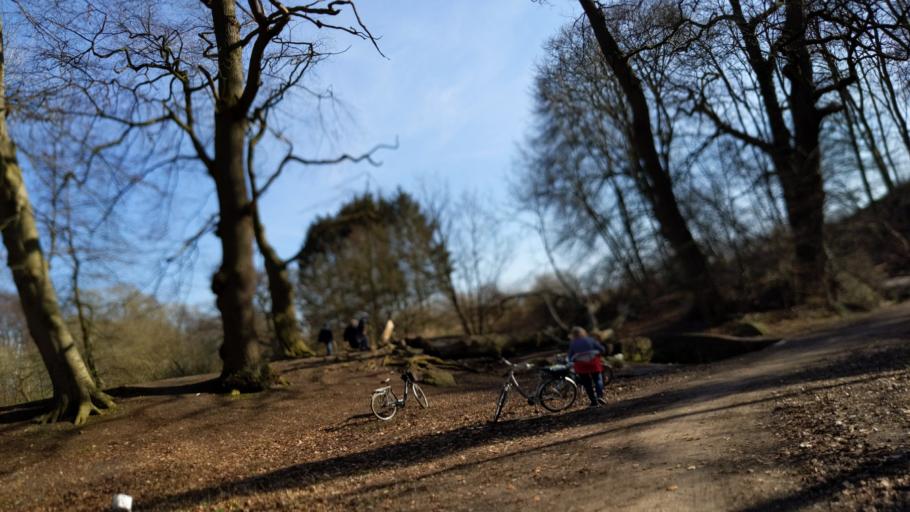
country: DE
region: Schleswig-Holstein
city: Travemuende
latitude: 53.9840
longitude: 10.8260
